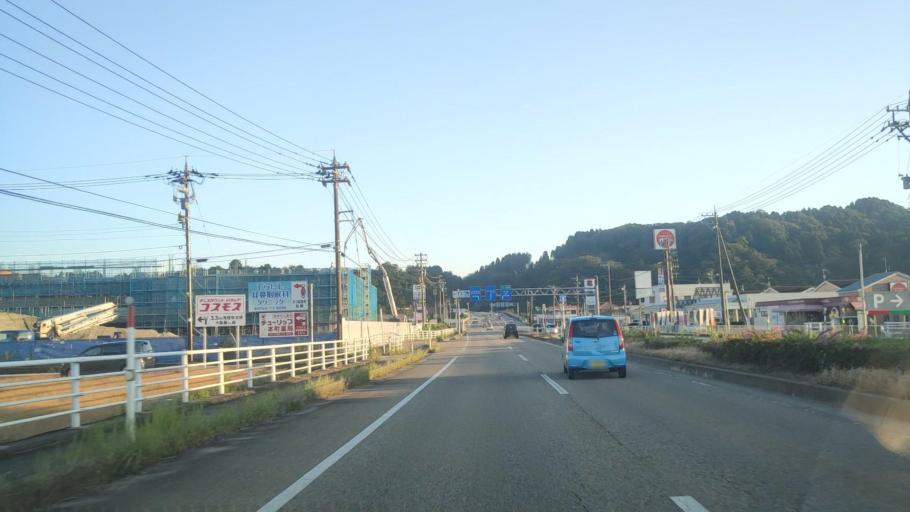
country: JP
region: Toyama
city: Himi
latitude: 36.8597
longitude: 136.9759
